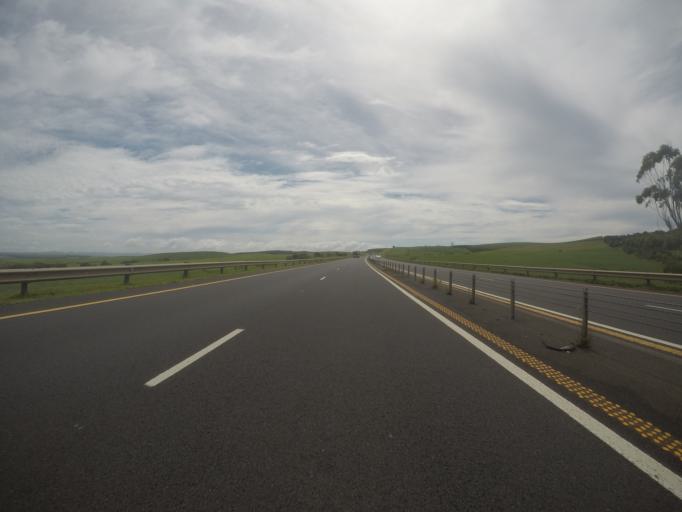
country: ZA
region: KwaZulu-Natal
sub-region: uThungulu District Municipality
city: Eshowe
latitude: -29.0539
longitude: 31.6331
